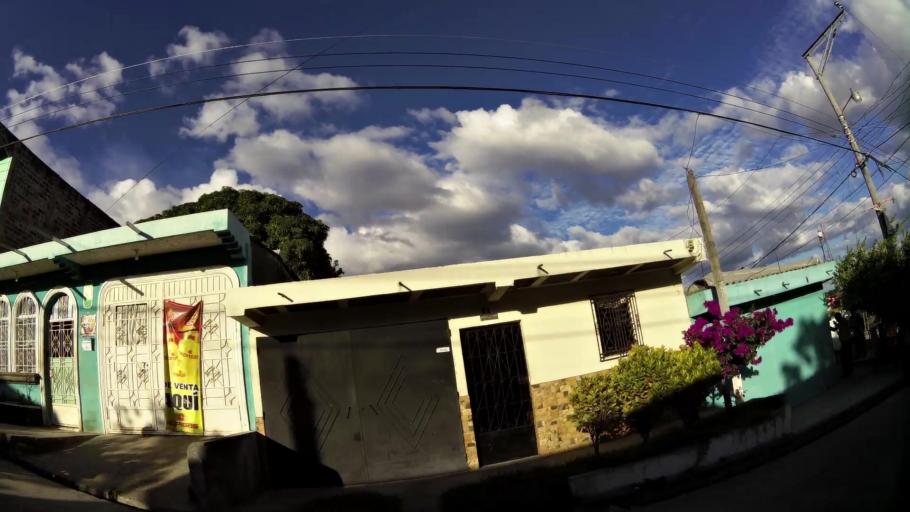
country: SV
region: Cuscatlan
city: Cojutepeque
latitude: 13.7132
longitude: -88.9306
